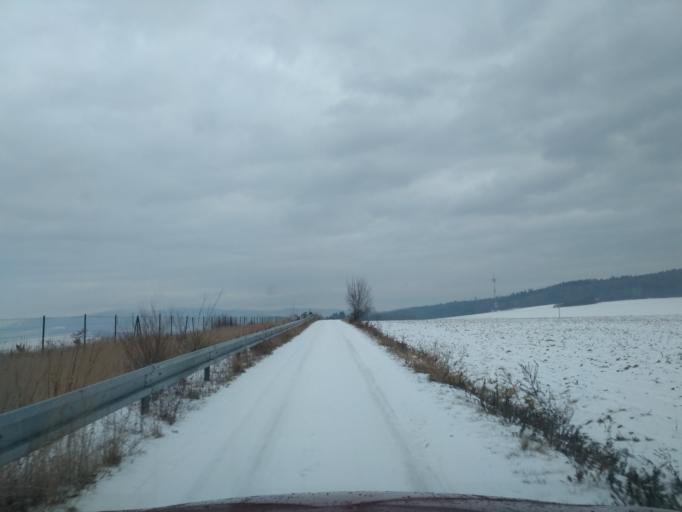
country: SK
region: Presovsky
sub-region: Okres Presov
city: Presov
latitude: 49.0058
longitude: 21.1465
